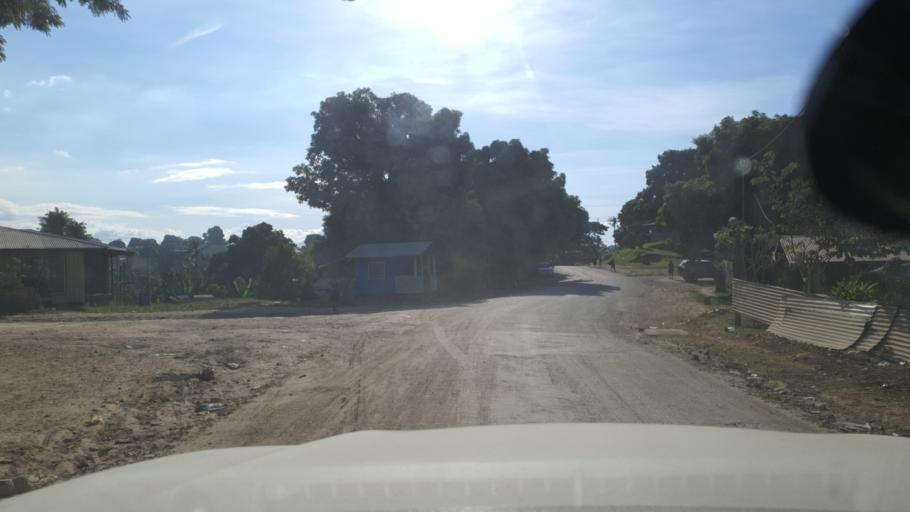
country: SB
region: Guadalcanal
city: Honiara
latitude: -9.4529
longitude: 159.9900
